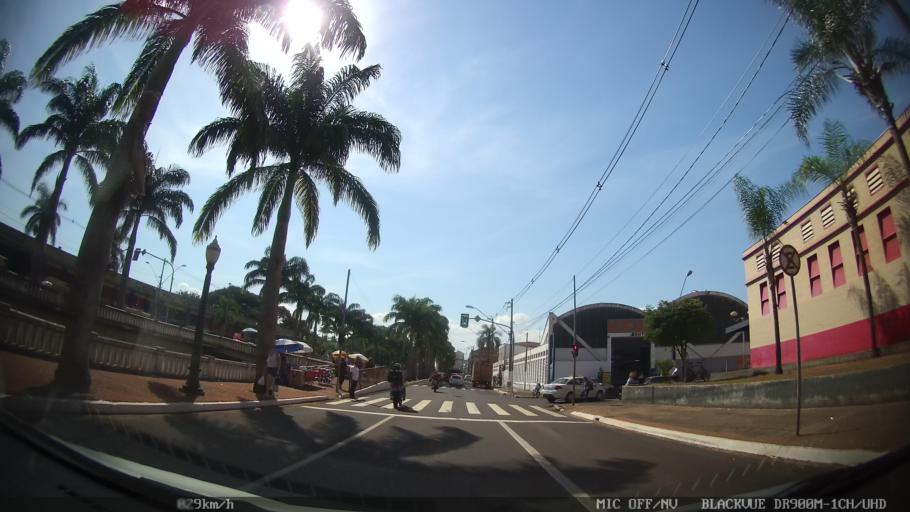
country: BR
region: Sao Paulo
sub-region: Ribeirao Preto
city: Ribeirao Preto
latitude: -21.1746
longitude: -47.8139
